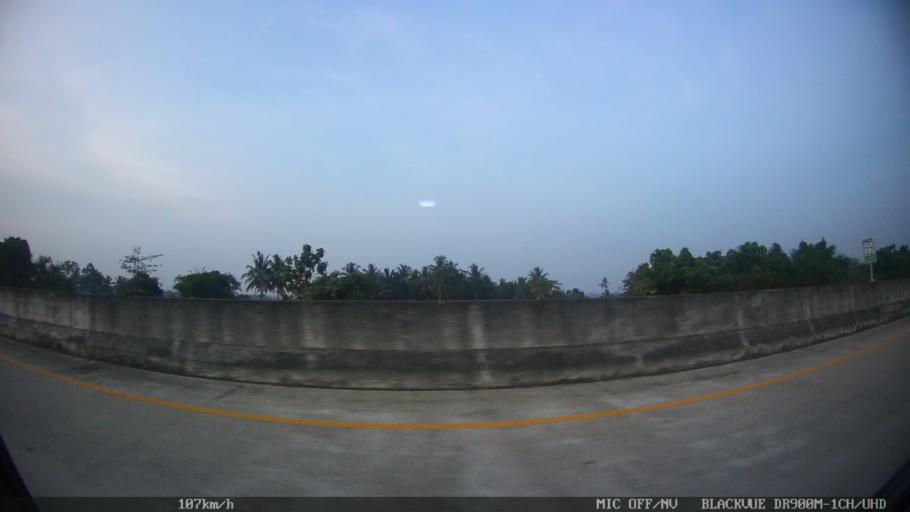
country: ID
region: Lampung
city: Pasuruan
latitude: -5.7158
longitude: 105.6564
